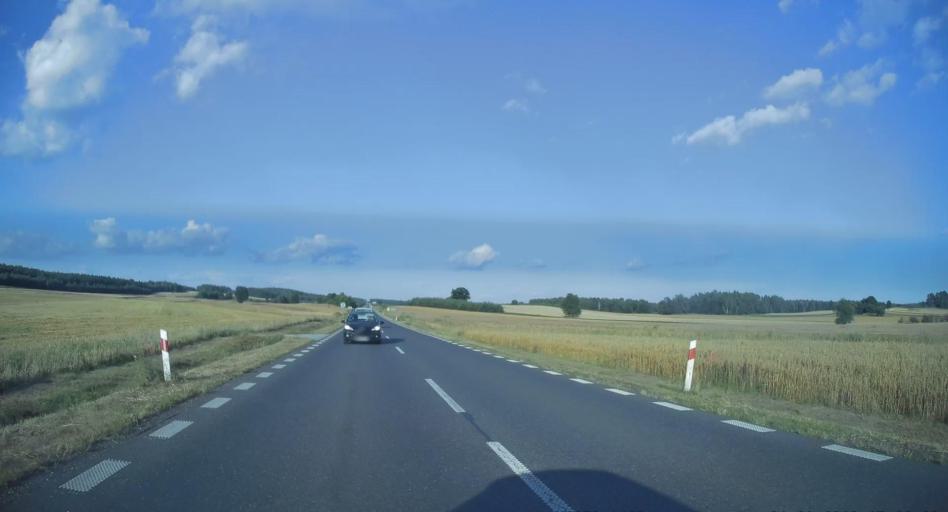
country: PL
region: Lodz Voivodeship
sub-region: Powiat rawski
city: Regnow
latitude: 51.7850
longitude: 20.3300
